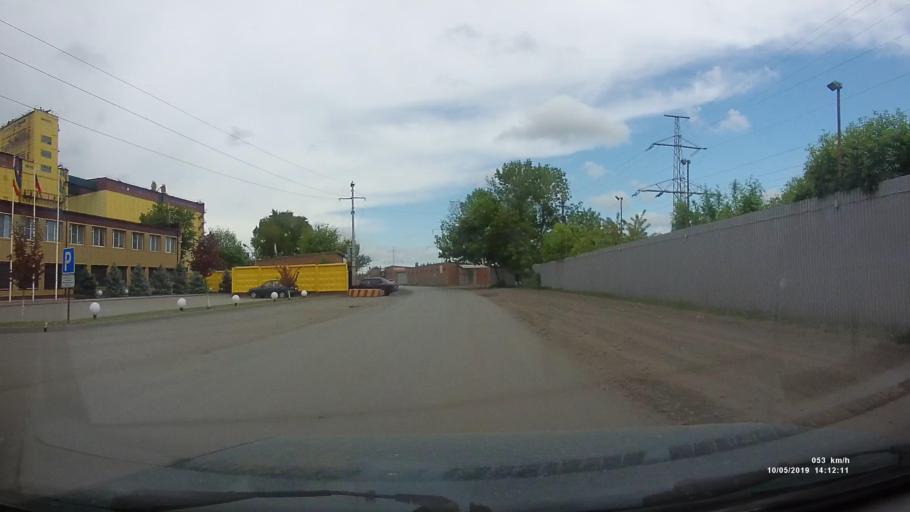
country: RU
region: Rostov
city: Azov
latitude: 47.0931
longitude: 39.4233
